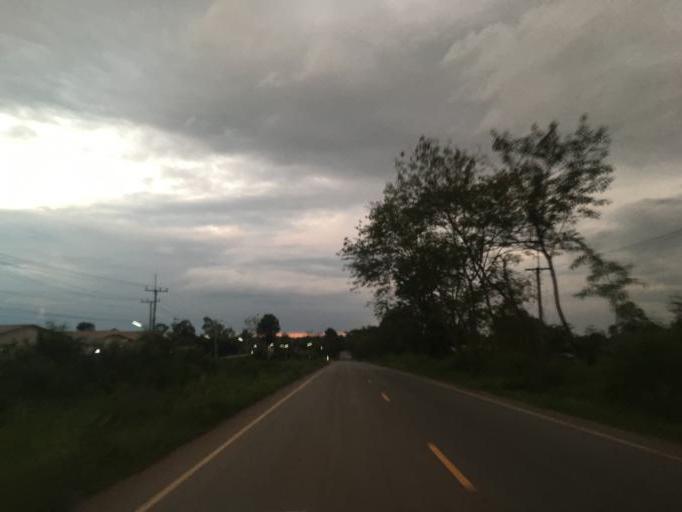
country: TH
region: Changwat Udon Thani
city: Nong Saeng
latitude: 17.2861
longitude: 102.7063
